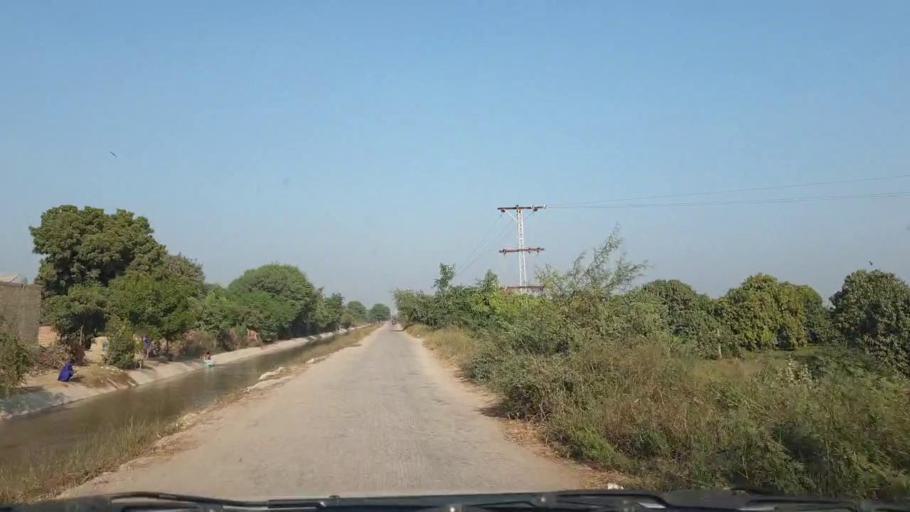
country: PK
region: Sindh
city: Tando Muhammad Khan
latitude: 25.2160
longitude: 68.6256
